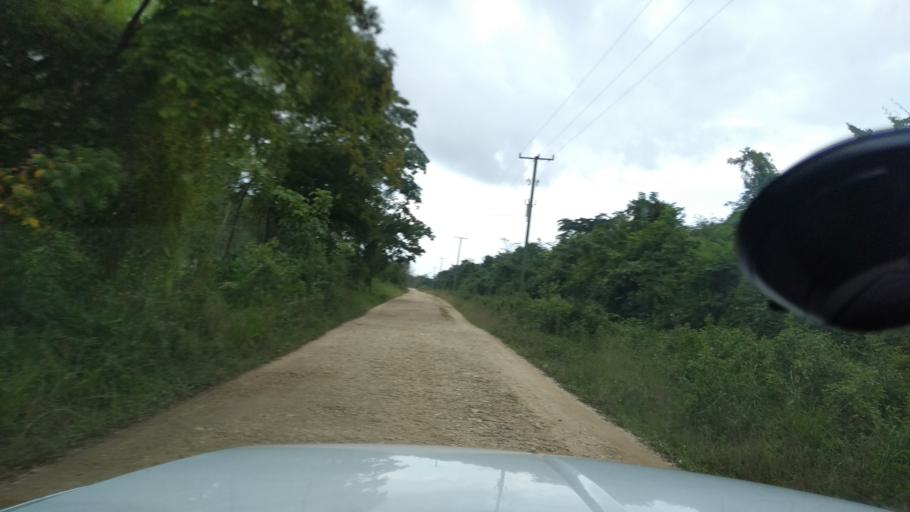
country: BZ
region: Toledo
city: Punta Gorda
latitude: 16.2140
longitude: -89.0131
